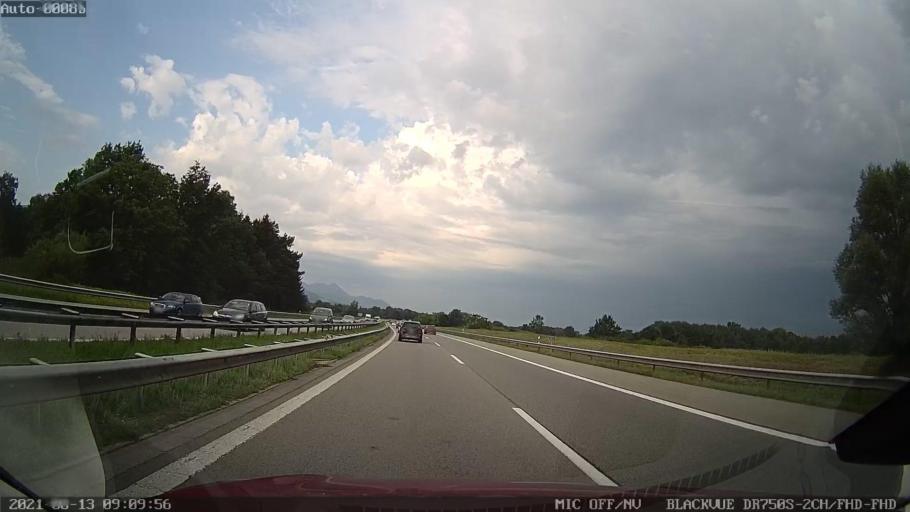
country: DE
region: Bavaria
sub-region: Upper Bavaria
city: Ubersee
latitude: 47.8365
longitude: 12.4500
